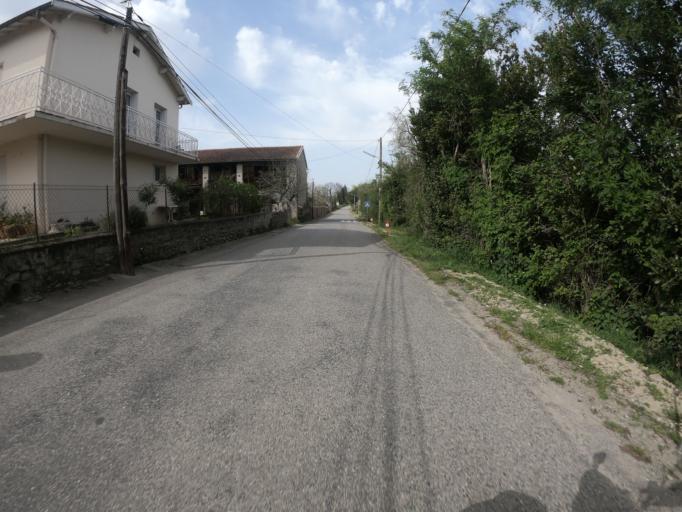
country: FR
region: Midi-Pyrenees
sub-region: Departement de l'Ariege
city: La Tour-du-Crieu
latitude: 43.1118
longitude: 1.7230
